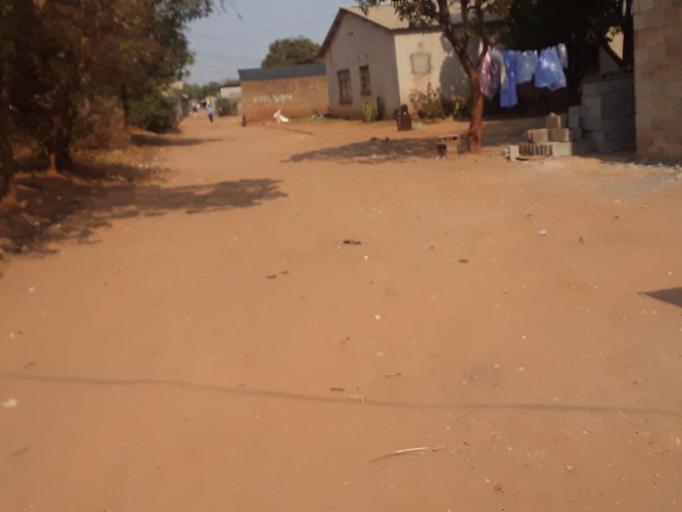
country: ZM
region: Lusaka
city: Lusaka
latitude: -15.3535
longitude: 28.2983
